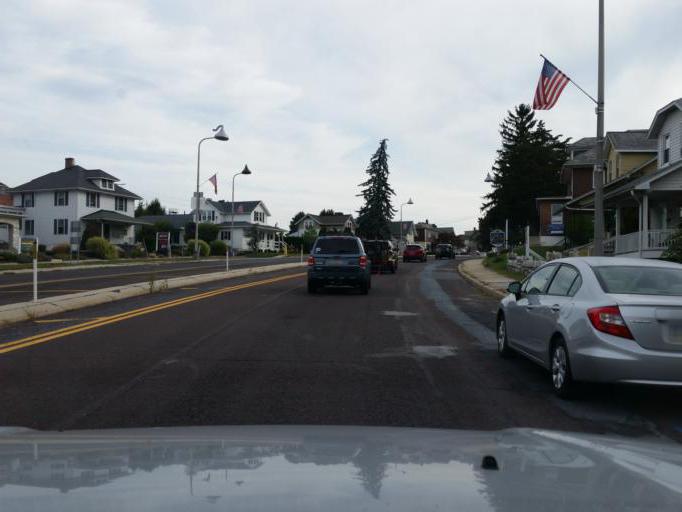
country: US
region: Pennsylvania
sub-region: Dauphin County
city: Hershey
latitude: 40.2808
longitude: -76.6621
